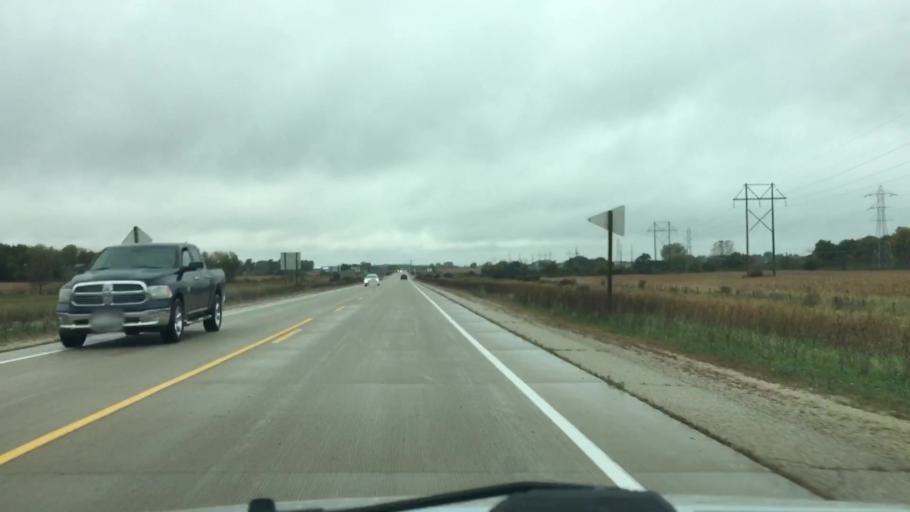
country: US
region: Wisconsin
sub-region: Walworth County
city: Whitewater
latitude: 42.8198
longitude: -88.7055
